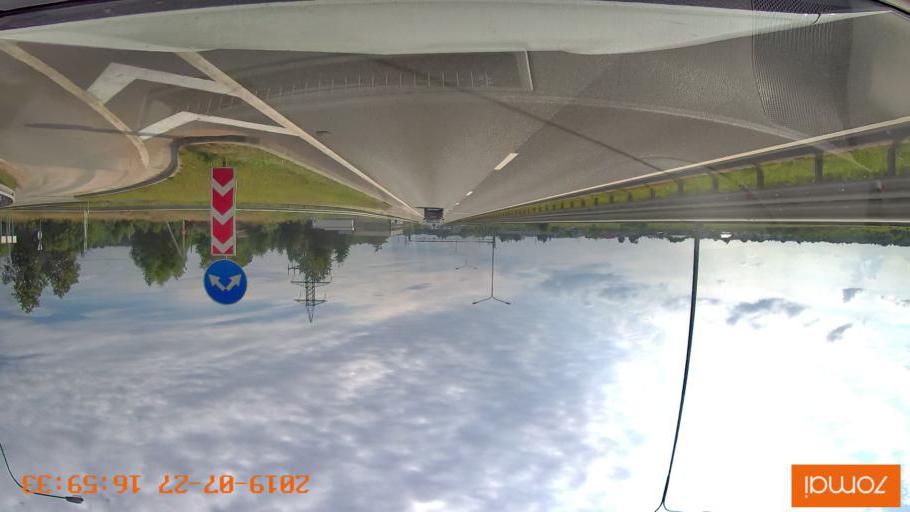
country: RU
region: Kaliningrad
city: Bol'shoe Isakovo
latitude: 54.7045
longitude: 20.6462
